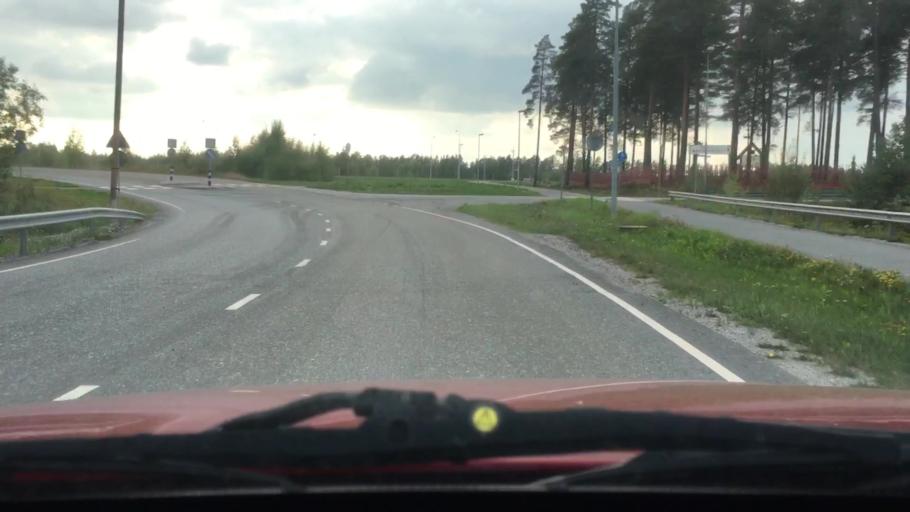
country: FI
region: Varsinais-Suomi
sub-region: Turku
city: Masku
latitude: 60.5491
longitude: 22.1274
